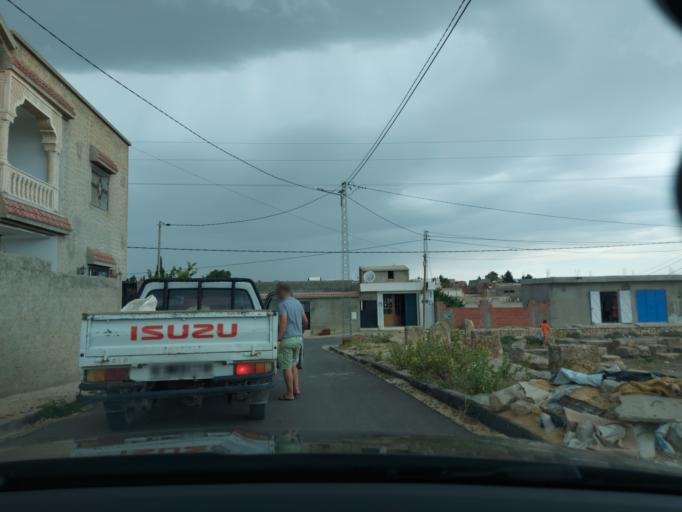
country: TN
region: Silyanah
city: Maktar
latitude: 35.8535
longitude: 9.1982
